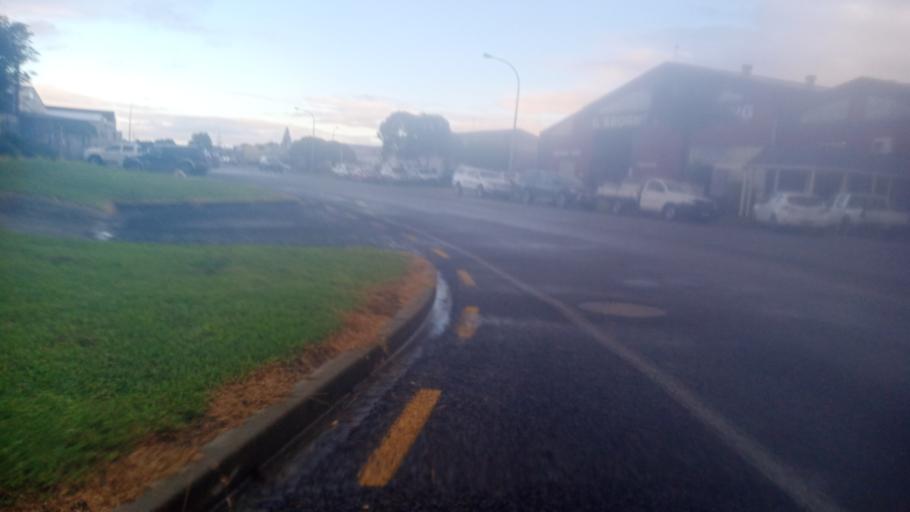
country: NZ
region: Gisborne
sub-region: Gisborne District
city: Gisborne
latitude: -38.6672
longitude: 177.9972
